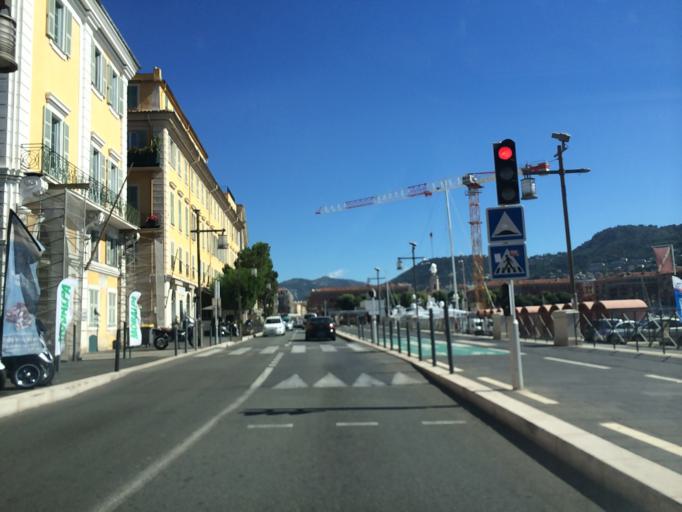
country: FR
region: Provence-Alpes-Cote d'Azur
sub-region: Departement des Alpes-Maritimes
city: Nice
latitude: 43.6954
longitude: 7.2833
